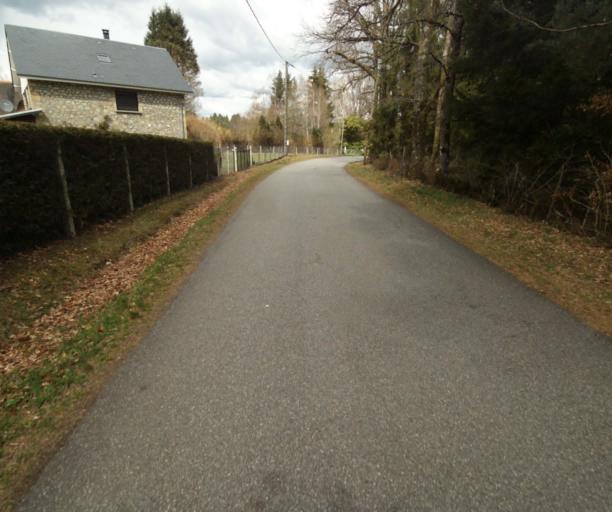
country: FR
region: Limousin
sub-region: Departement de la Correze
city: Correze
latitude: 45.3312
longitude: 1.9176
